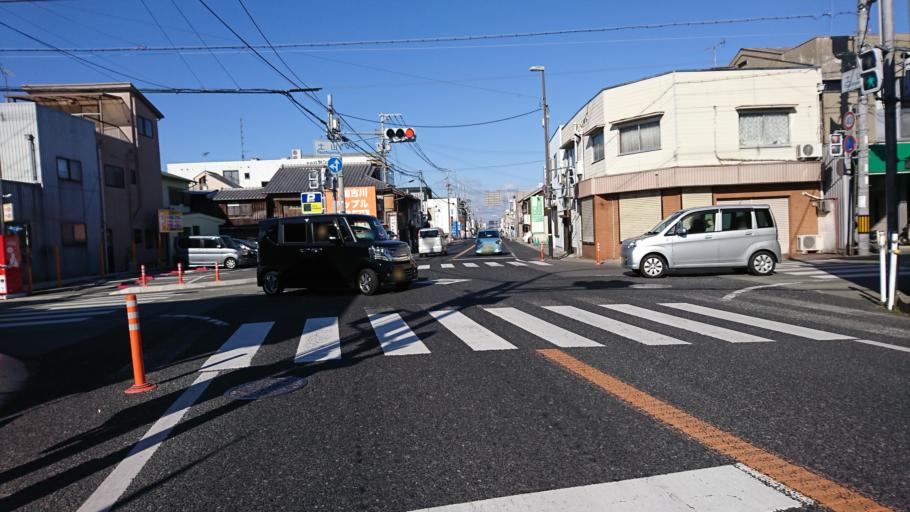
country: JP
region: Hyogo
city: Kakogawacho-honmachi
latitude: 34.7217
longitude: 134.8908
